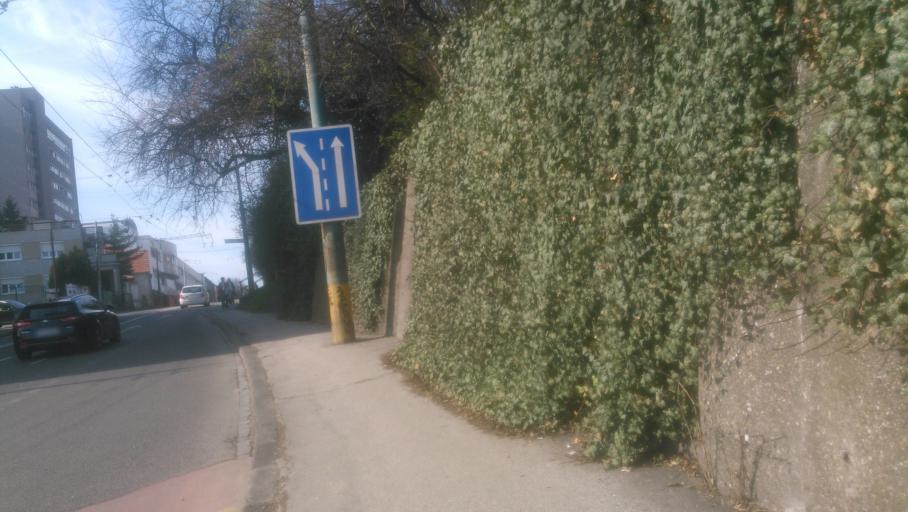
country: SK
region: Bratislavsky
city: Bratislava
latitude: 48.1638
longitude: 17.0981
